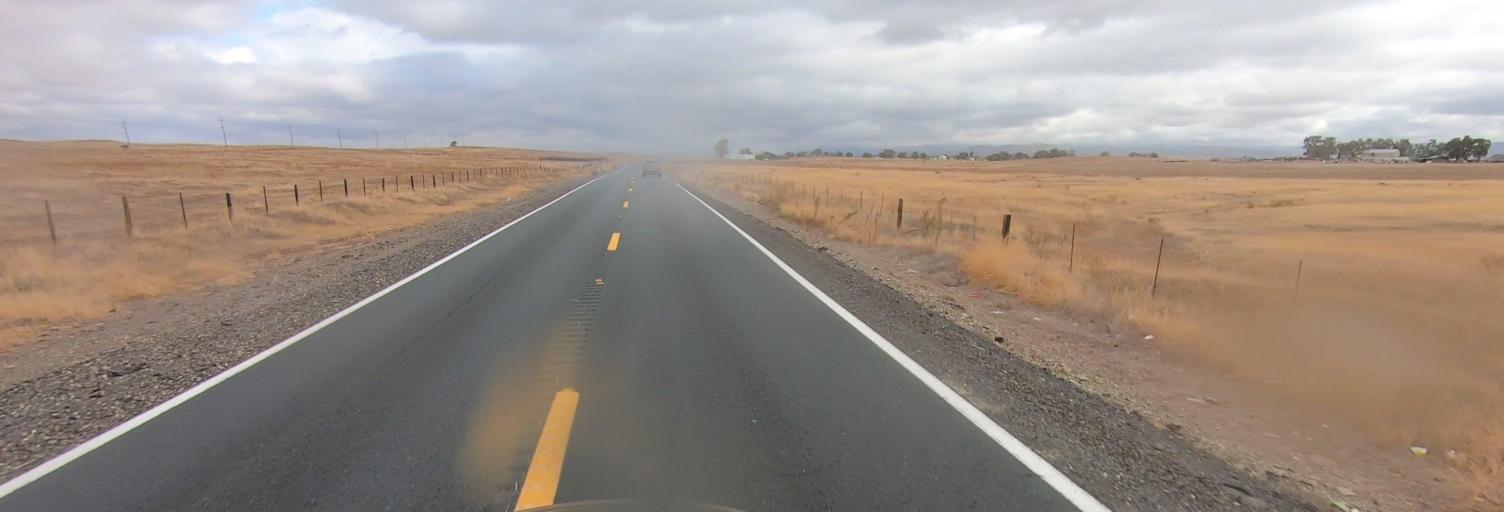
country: US
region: California
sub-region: Calaveras County
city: Rancho Calaveras
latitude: 38.0865
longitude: -120.9571
